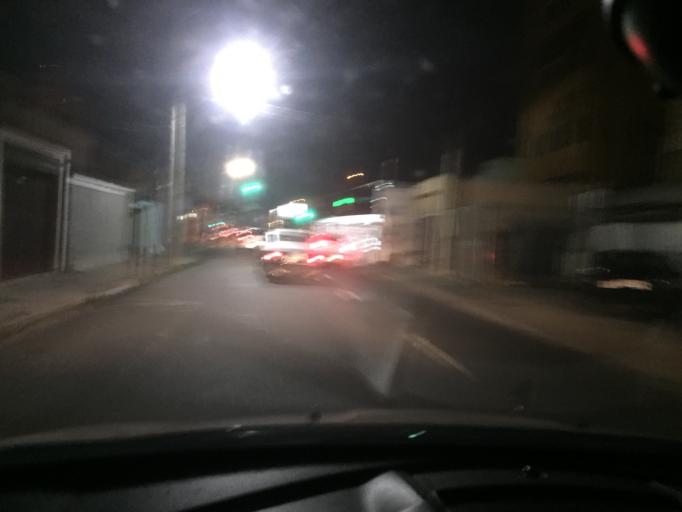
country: BR
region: Sao Paulo
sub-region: Jundiai
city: Jundiai
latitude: -23.2045
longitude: -46.8660
